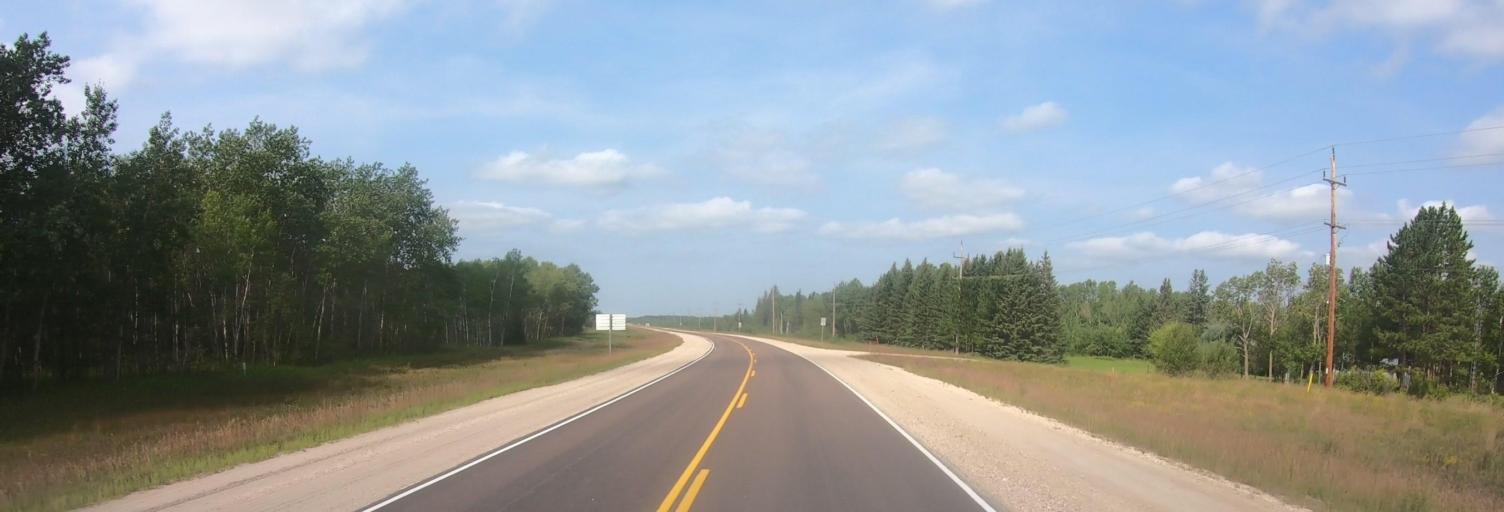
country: CA
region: Manitoba
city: La Broquerie
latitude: 49.2668
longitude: -96.3693
